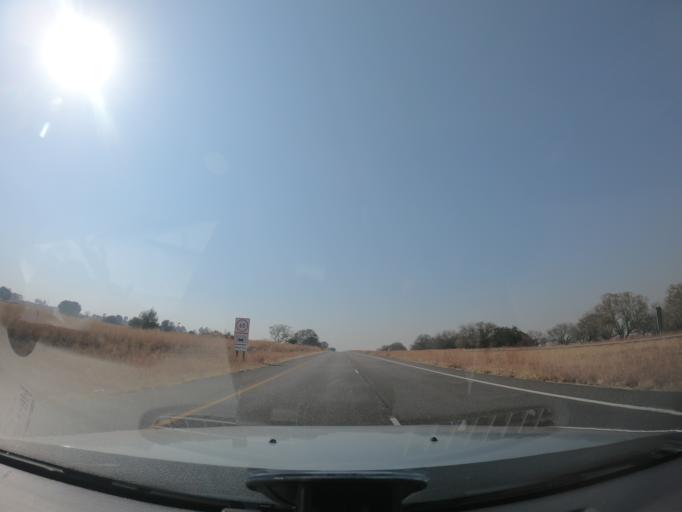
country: ZA
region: Gauteng
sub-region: City of Tshwane Metropolitan Municipality
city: Bronkhorstspruit
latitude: -25.7992
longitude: 28.6285
